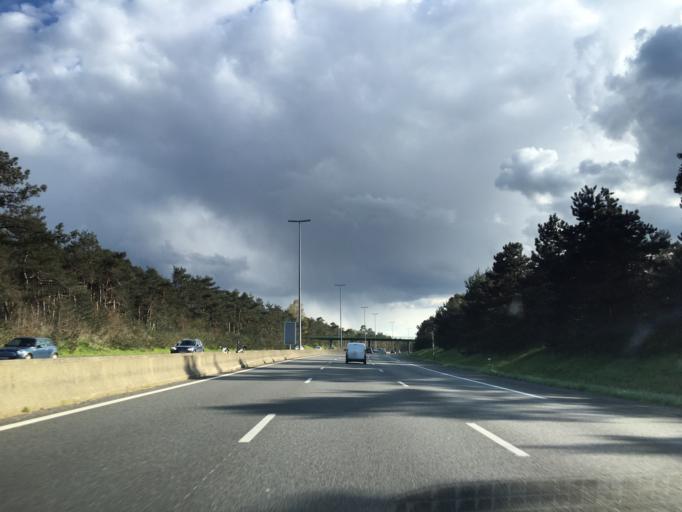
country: FR
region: Picardie
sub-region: Departement de l'Oise
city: Thiers-sur-Theve
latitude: 49.1682
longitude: 2.5993
